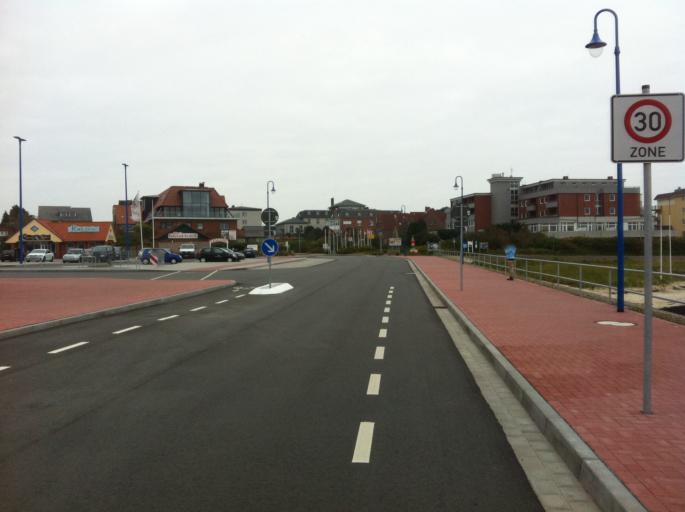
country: DE
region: Schleswig-Holstein
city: Wittdun
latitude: 54.6283
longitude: 8.3965
